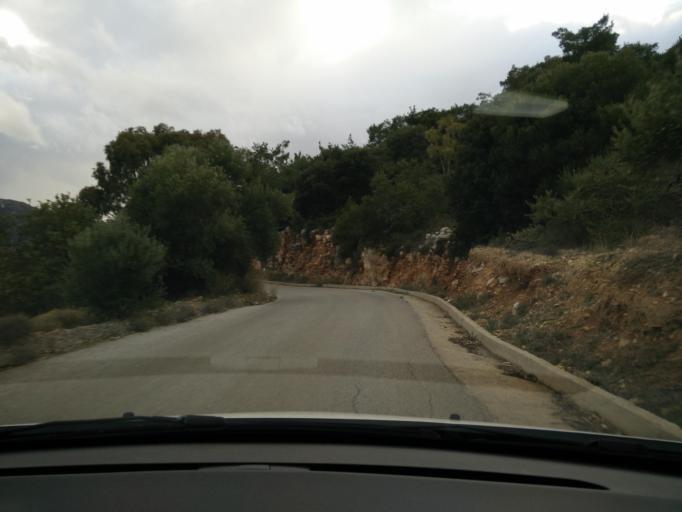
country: GR
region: Crete
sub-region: Nomos Lasithiou
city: Kritsa
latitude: 35.1049
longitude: 25.6950
